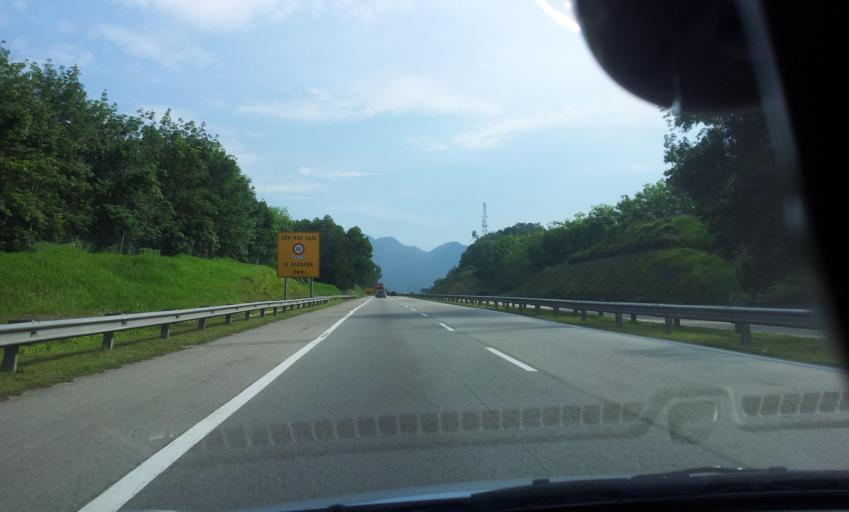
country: MY
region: Pahang
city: Bentong Town
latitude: 3.4563
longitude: 102.0385
